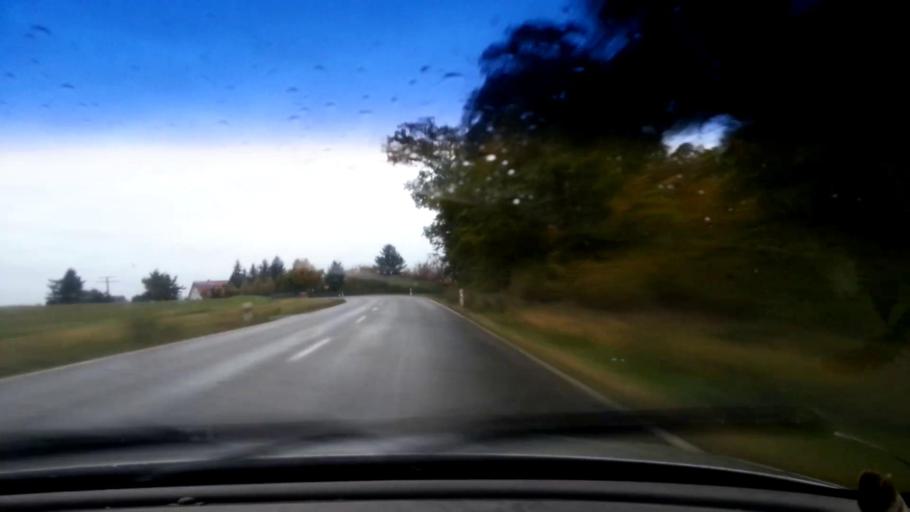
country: DE
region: Bavaria
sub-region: Upper Franconia
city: Viereth-Trunstadt
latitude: 49.8978
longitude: 10.7753
